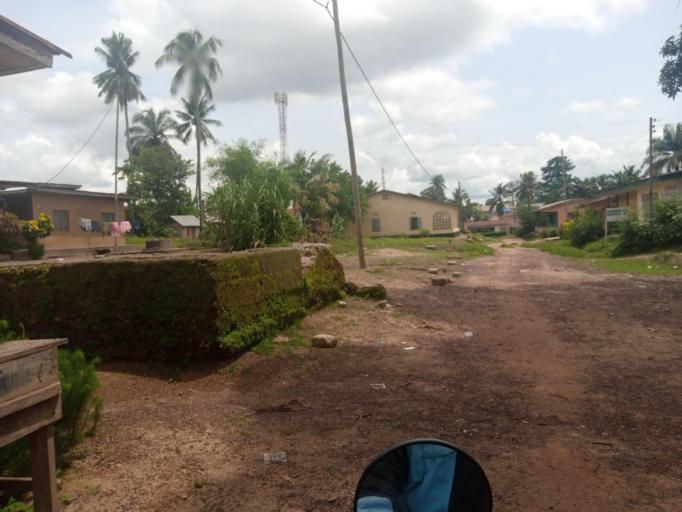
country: SL
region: Southern Province
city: Bo
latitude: 7.9568
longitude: -11.7387
